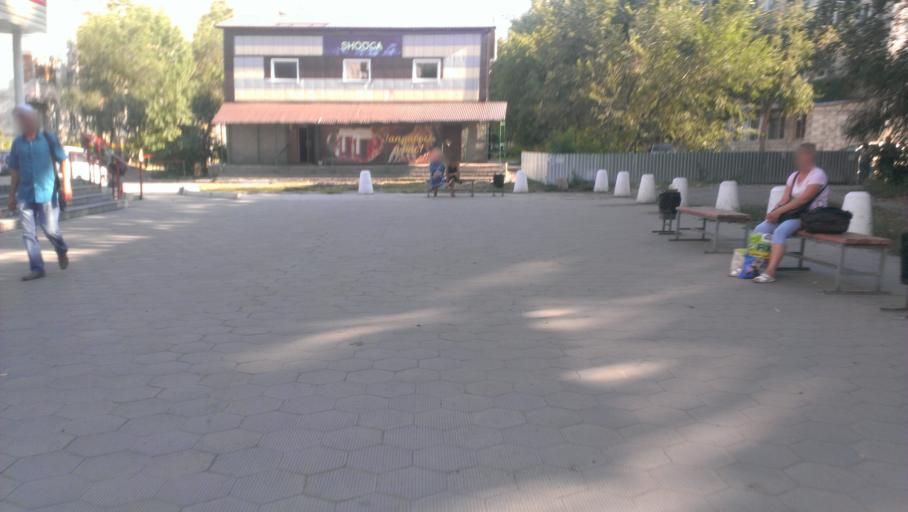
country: RU
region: Altai Krai
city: Novosilikatnyy
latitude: 53.3066
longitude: 83.6213
